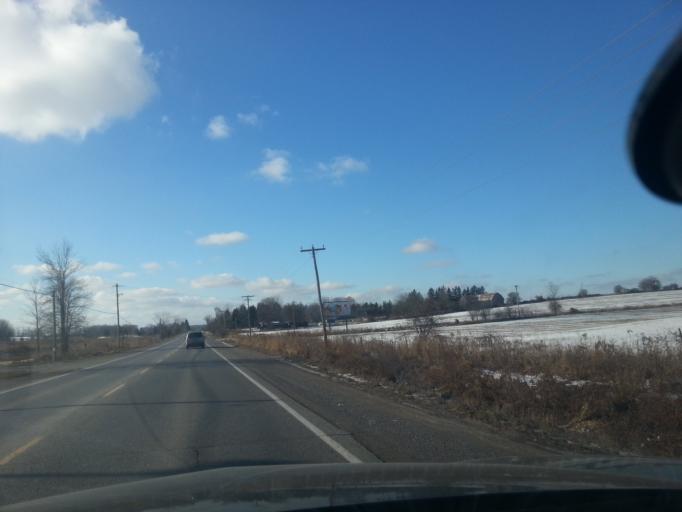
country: CA
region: Ontario
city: Peterborough
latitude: 44.2713
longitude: -78.3899
